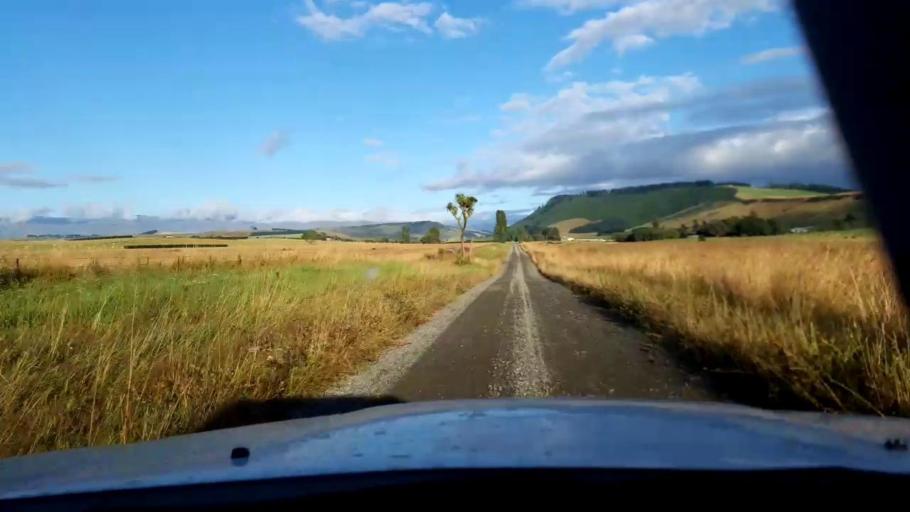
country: NZ
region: Canterbury
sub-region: Timaru District
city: Timaru
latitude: -44.4265
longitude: 171.1166
